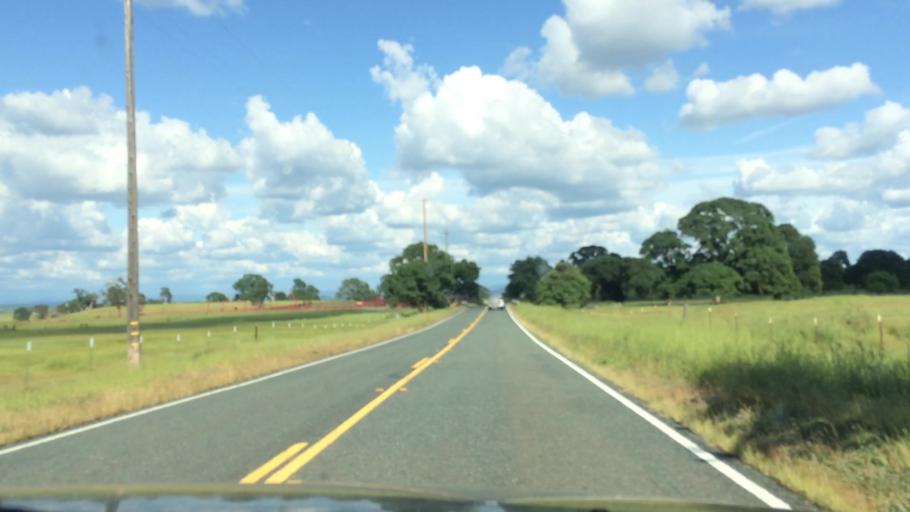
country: US
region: California
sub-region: Amador County
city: Ione
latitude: 38.3860
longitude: -121.0461
